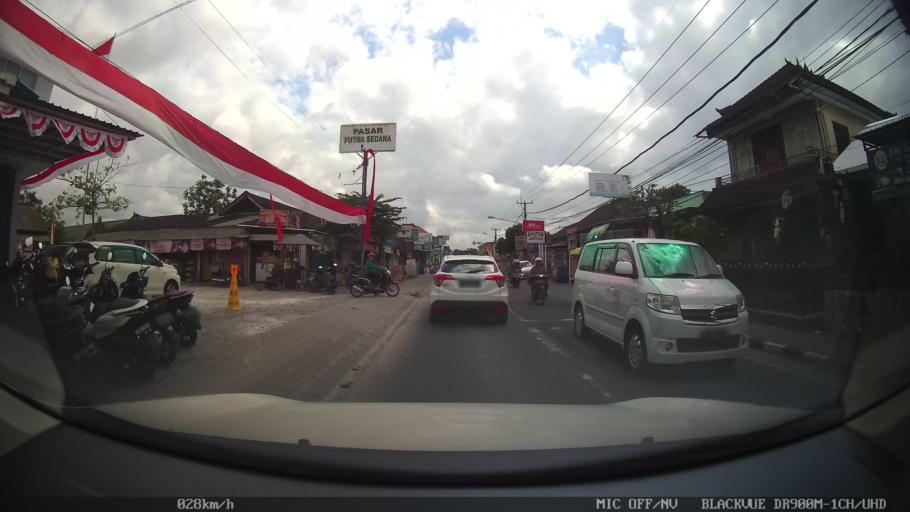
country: ID
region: Bali
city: Banjar Karangsuling
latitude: -8.5994
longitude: 115.1733
